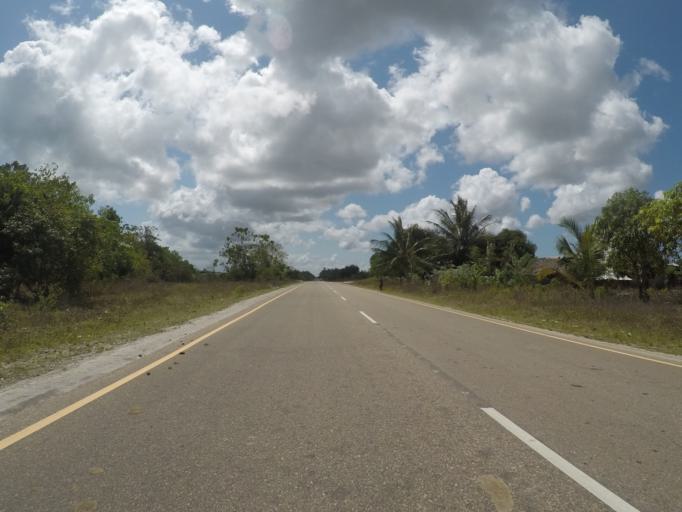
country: TZ
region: Zanzibar Central/South
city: Koani
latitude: -6.2669
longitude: 39.3614
